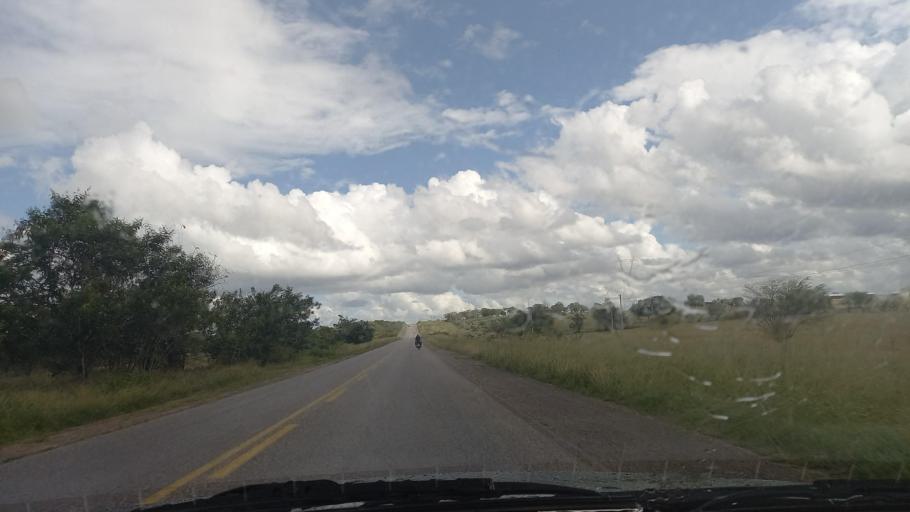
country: BR
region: Pernambuco
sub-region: Lajedo
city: Lajedo
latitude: -8.5821
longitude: -36.2881
